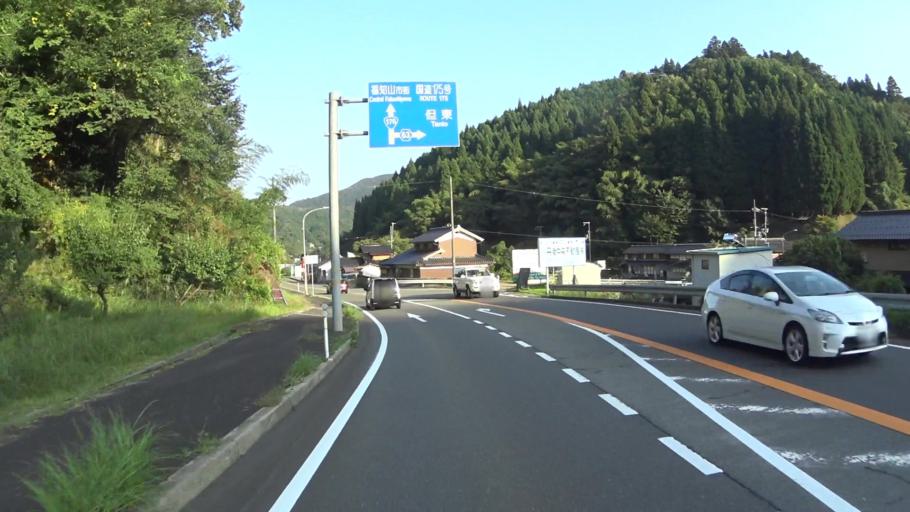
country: JP
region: Kyoto
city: Fukuchiyama
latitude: 35.4242
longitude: 135.0737
